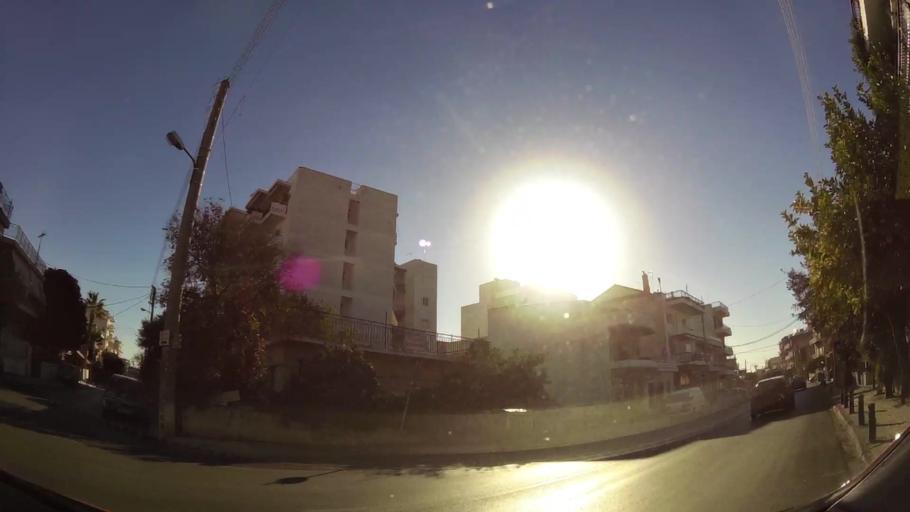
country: GR
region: Attica
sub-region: Nomarchia Anatolikis Attikis
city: Acharnes
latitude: 38.0896
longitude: 23.7356
